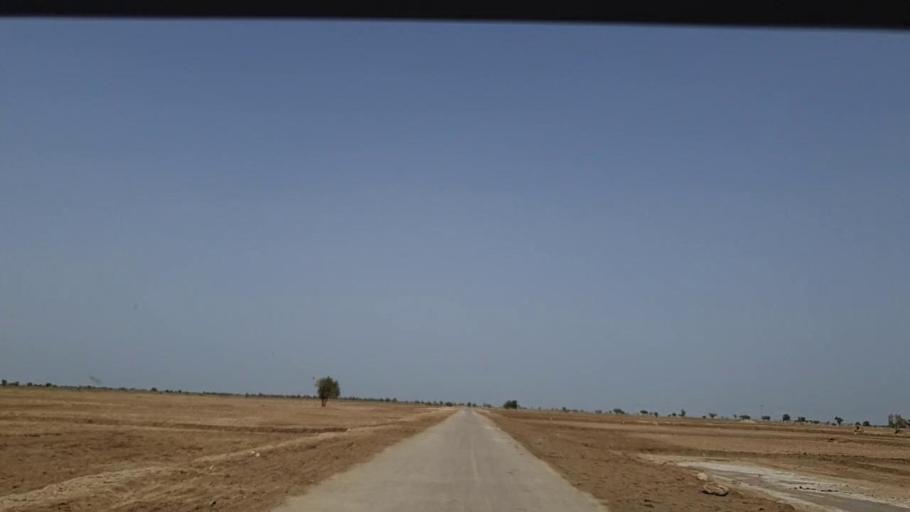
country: PK
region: Sindh
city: Johi
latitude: 26.7707
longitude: 67.6470
